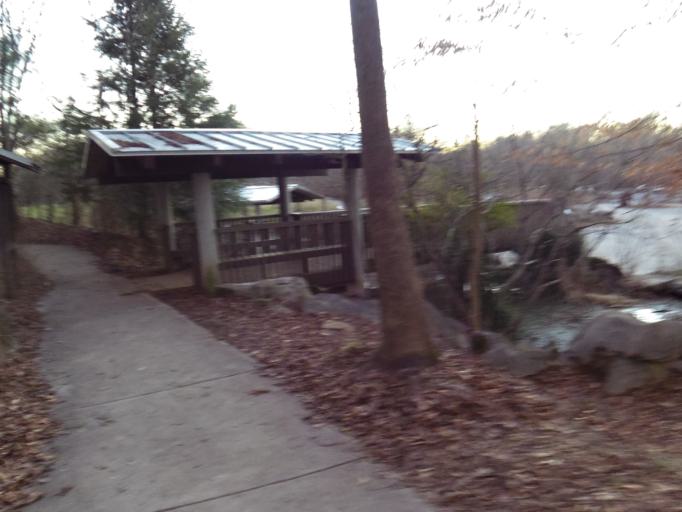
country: US
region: Tennessee
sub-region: Knox County
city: Knoxville
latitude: 35.9562
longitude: -83.8664
